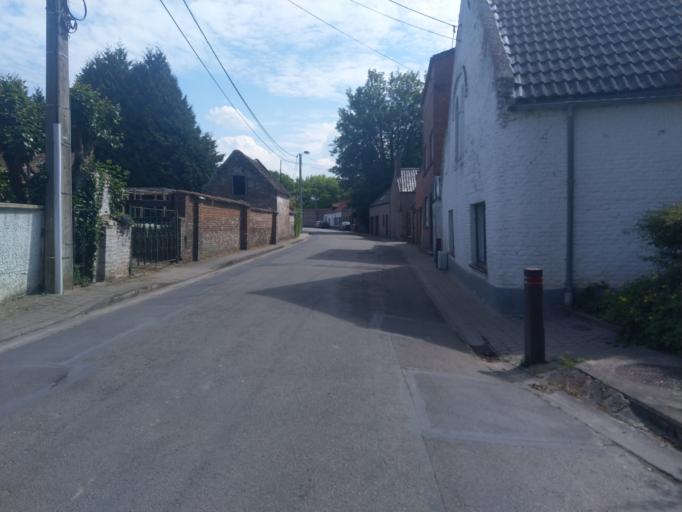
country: BE
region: Wallonia
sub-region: Province du Hainaut
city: Mons
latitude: 50.4409
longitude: 4.0015
